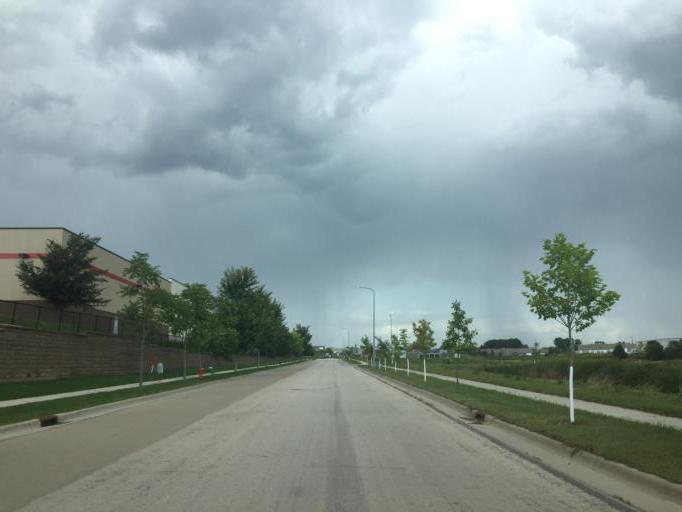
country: US
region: Minnesota
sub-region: Olmsted County
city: Rochester
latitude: 44.0462
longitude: -92.5161
